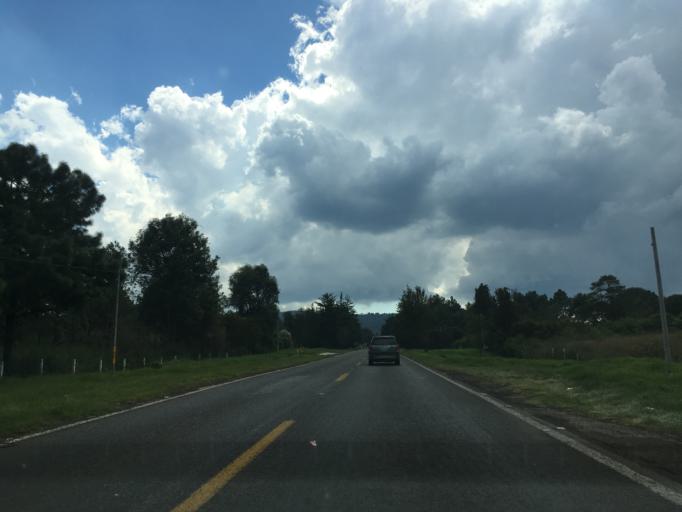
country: MX
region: Michoacan
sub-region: Patzcuaro
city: Santa Ana Chapitiro
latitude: 19.5179
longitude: -101.6652
